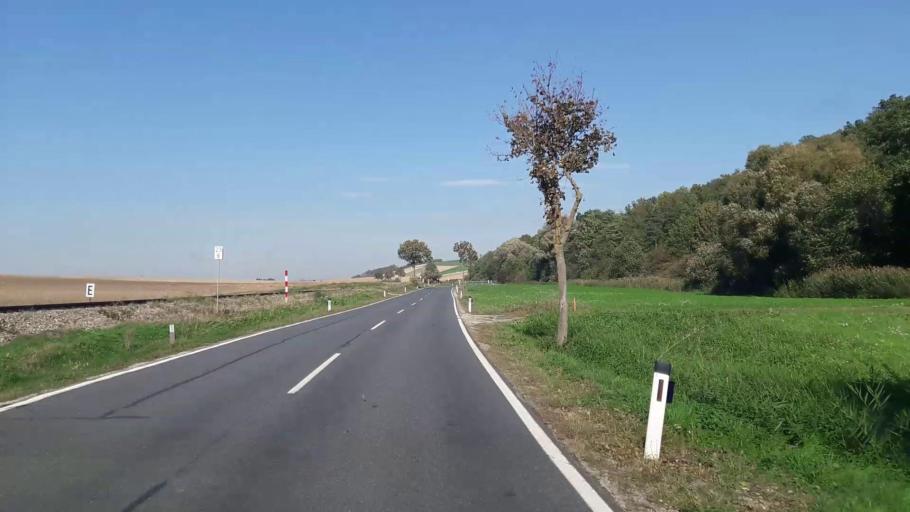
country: AT
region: Lower Austria
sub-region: Politischer Bezirk Korneuburg
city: Ernstbrunn
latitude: 48.4870
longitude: 16.3693
